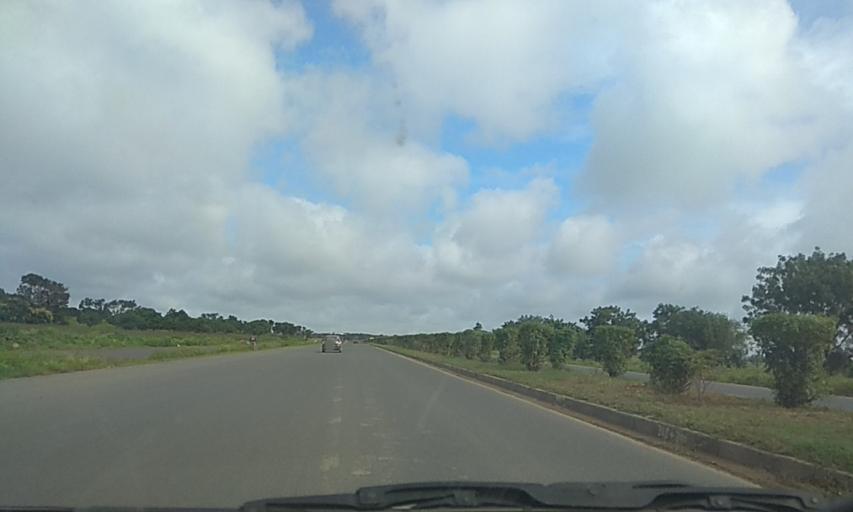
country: IN
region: Karnataka
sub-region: Haveri
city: Shiggaon
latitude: 14.9991
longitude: 75.2085
